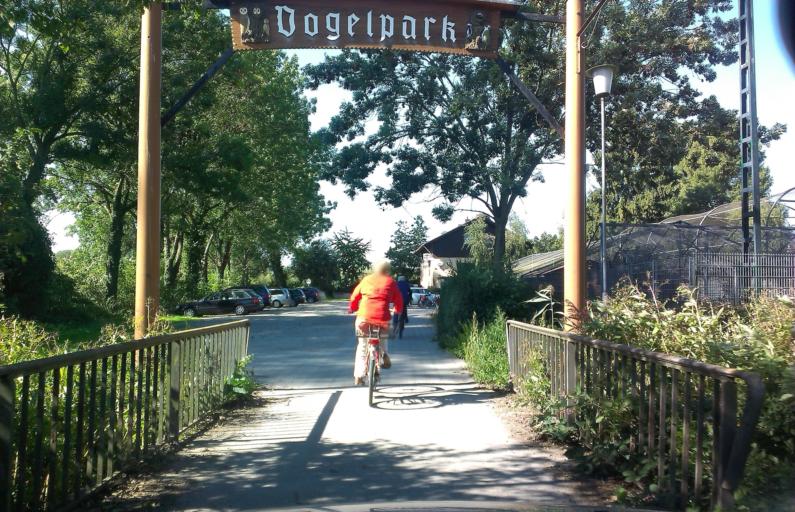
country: DE
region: Baden-Wuerttemberg
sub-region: Karlsruhe Region
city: Oberhausen-Rheinhausen
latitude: 49.2589
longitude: 8.4802
